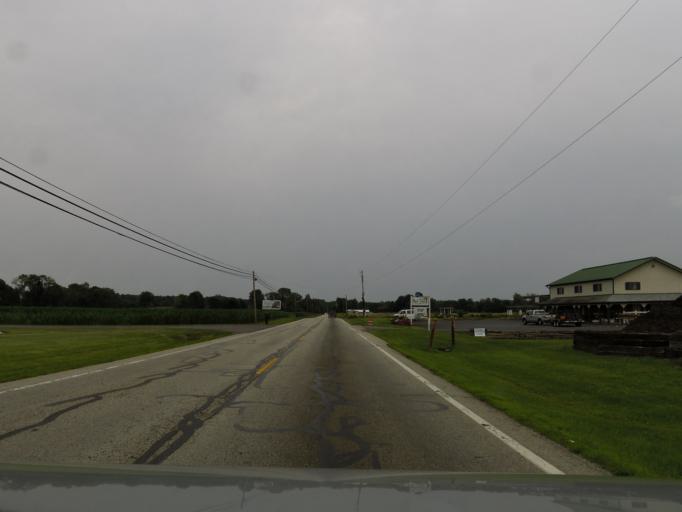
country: US
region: Ohio
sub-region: Clinton County
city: Wilmington
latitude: 39.4836
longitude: -83.9289
